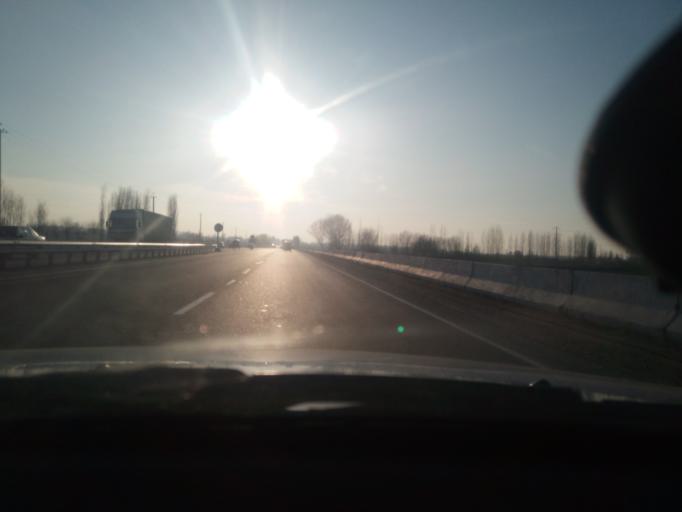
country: UZ
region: Toshkent
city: Urtaowul
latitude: 41.1892
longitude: 69.0914
